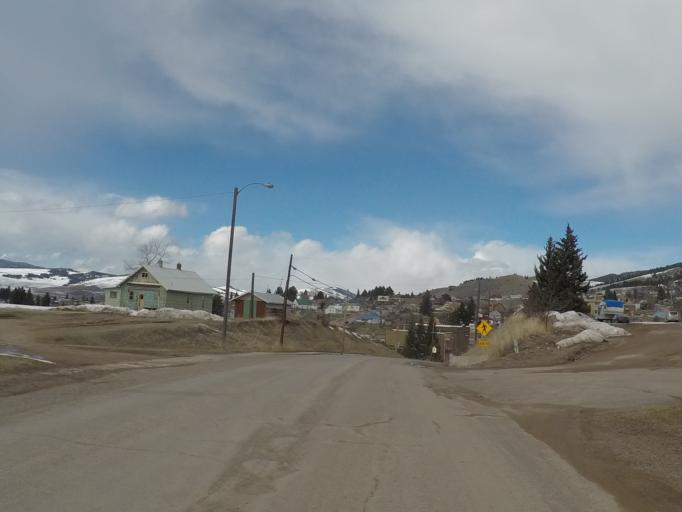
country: US
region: Montana
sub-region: Granite County
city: Philipsburg
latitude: 46.3299
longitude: -113.2949
